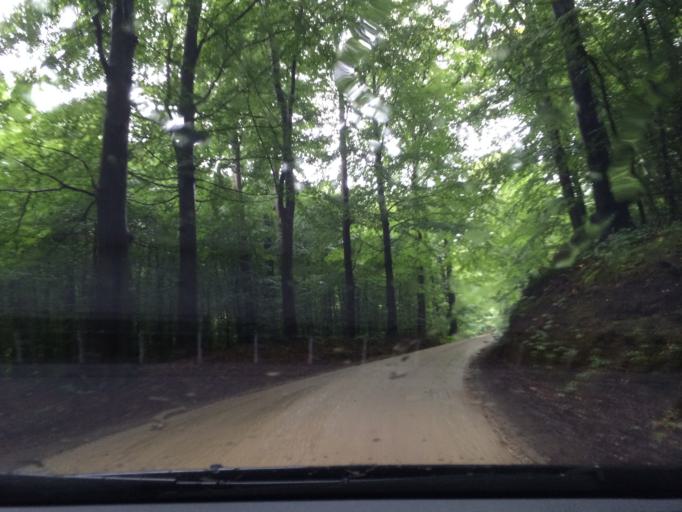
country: DK
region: Zealand
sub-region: Vordingborg Kommune
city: Stege
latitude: 54.9685
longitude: 12.5399
